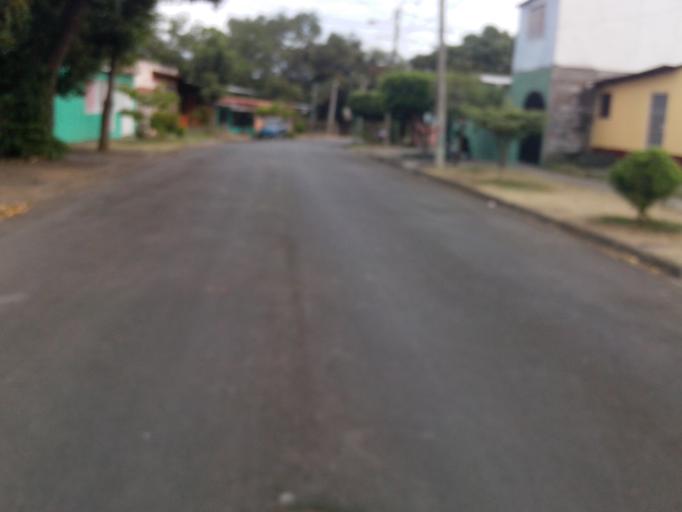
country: NI
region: Managua
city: Managua
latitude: 12.1159
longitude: -86.2041
